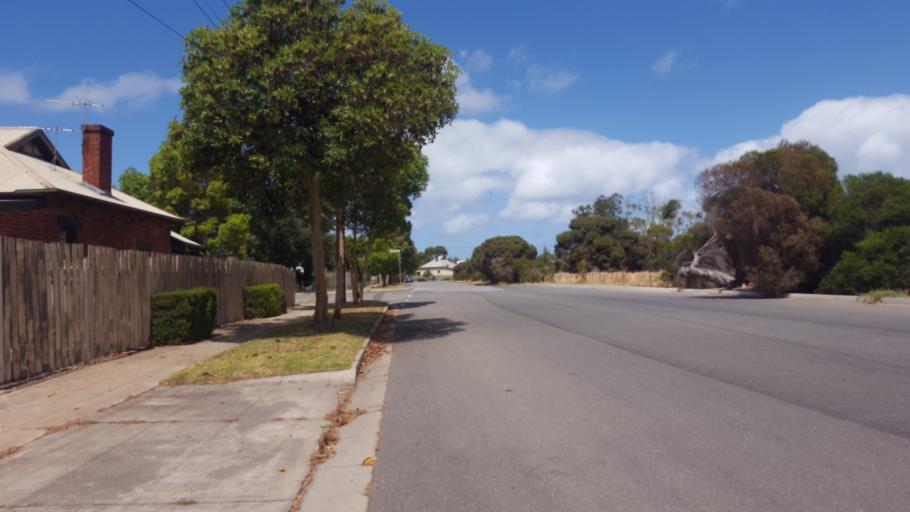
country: AU
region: South Australia
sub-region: Port Adelaide Enfield
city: Alberton
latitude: -34.8465
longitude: 138.5233
